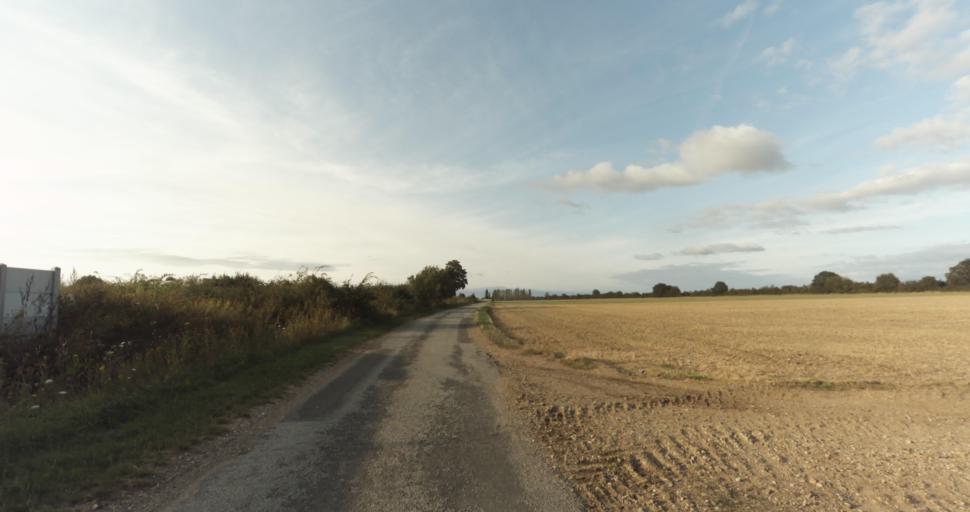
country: FR
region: Haute-Normandie
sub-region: Departement de l'Eure
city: Marcilly-sur-Eure
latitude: 48.8925
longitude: 1.2735
